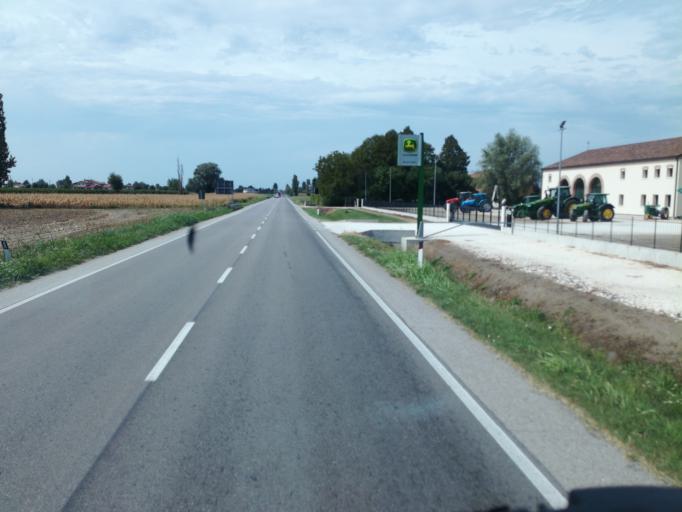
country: IT
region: Veneto
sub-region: Provincia di Padova
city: Arre
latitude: 45.2118
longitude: 11.9543
